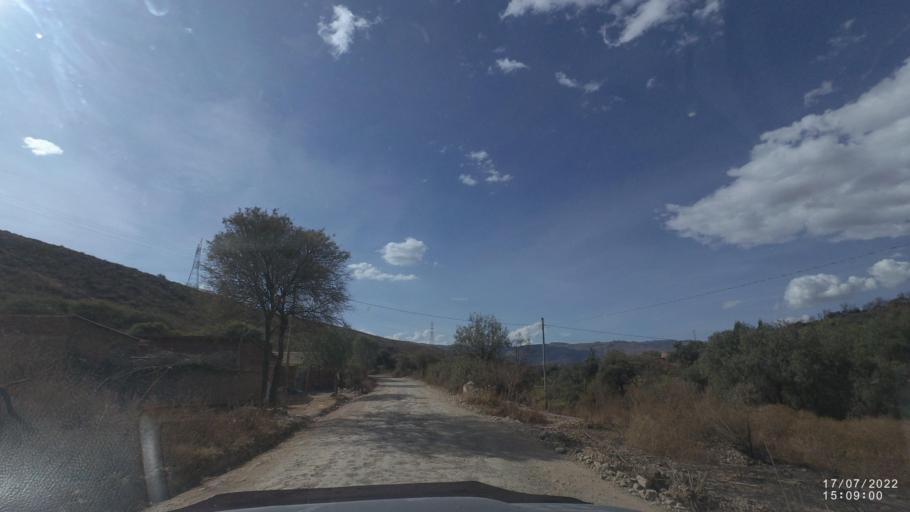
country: BO
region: Cochabamba
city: Capinota
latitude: -17.5766
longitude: -66.2666
